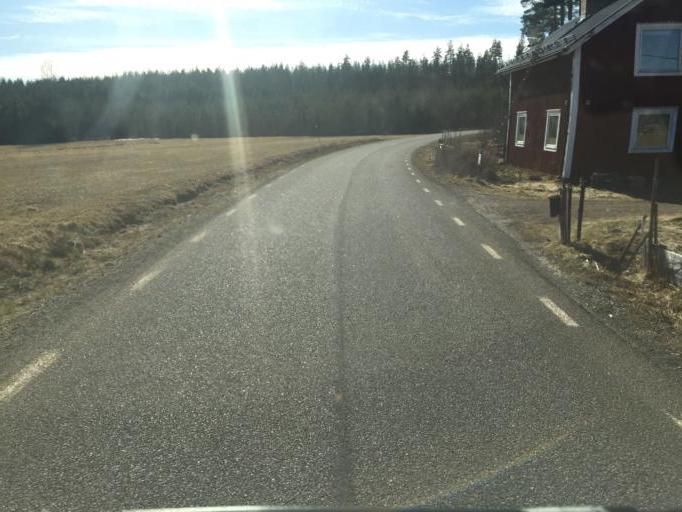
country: SE
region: Dalarna
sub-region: Vansbro Kommun
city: Vansbro
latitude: 60.4617
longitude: 13.9725
